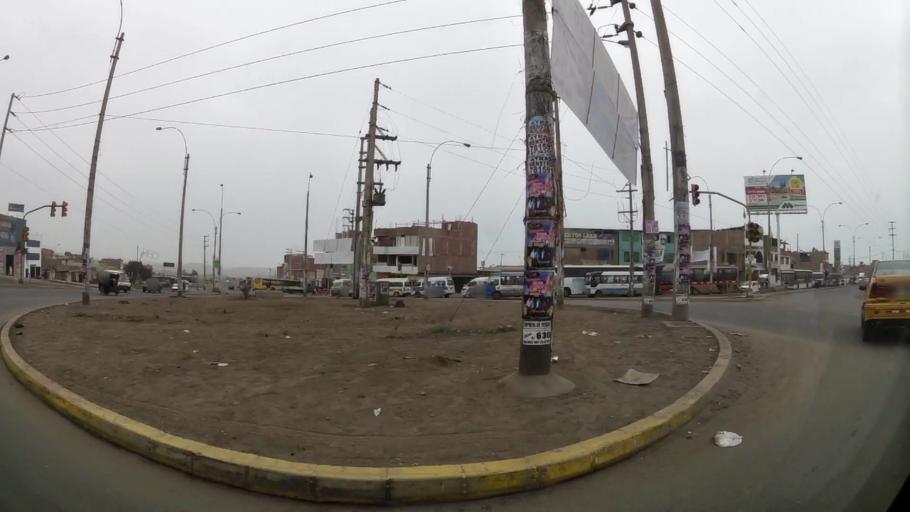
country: PE
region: Lima
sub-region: Lima
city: Punta Hermosa
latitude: -12.2397
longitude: -76.9124
